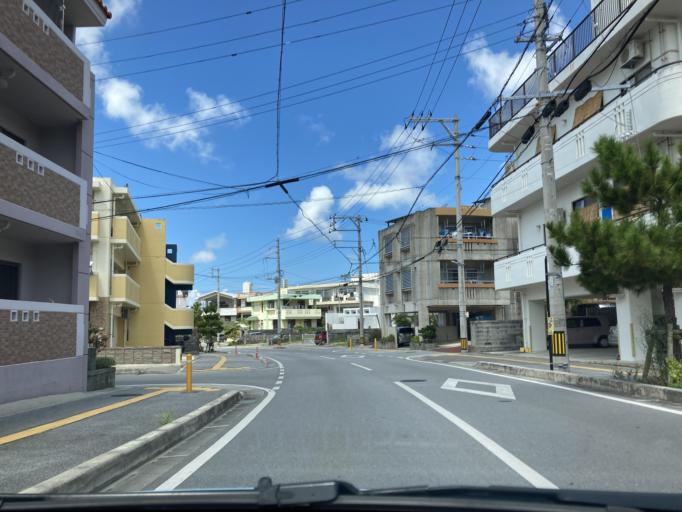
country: JP
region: Okinawa
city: Ginowan
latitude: 26.2199
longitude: 127.7330
